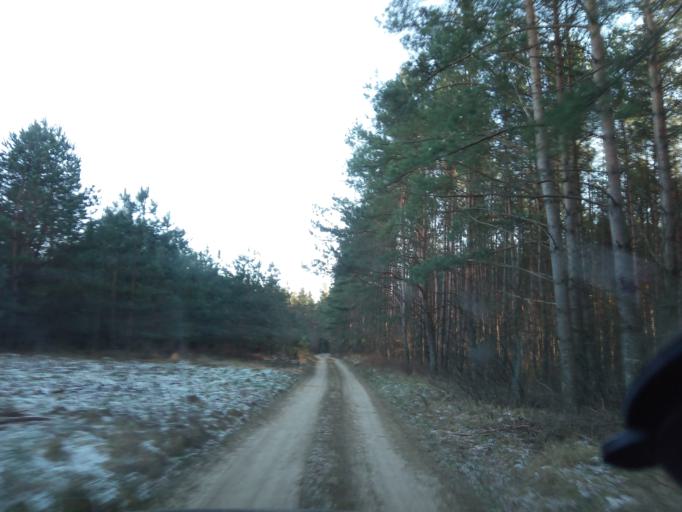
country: LT
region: Alytaus apskritis
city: Druskininkai
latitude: 53.9700
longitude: 23.9658
